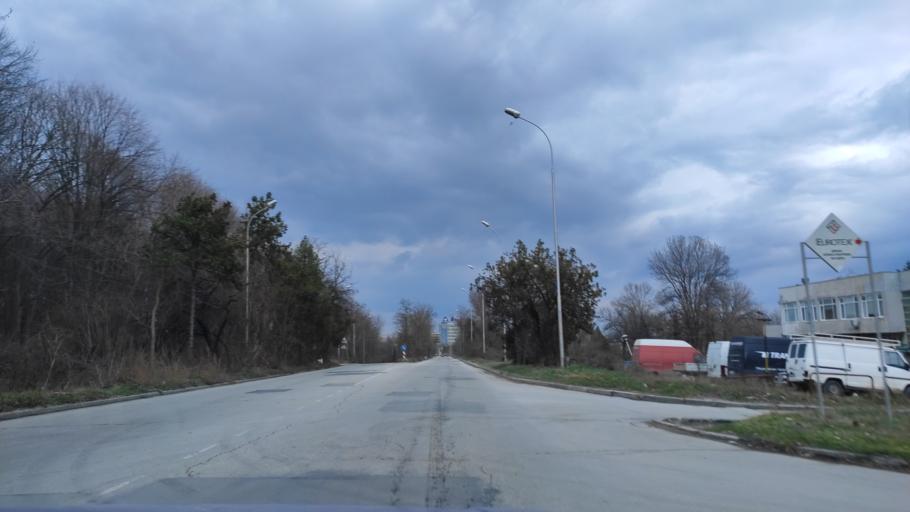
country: BG
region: Varna
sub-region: Obshtina Aksakovo
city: Aksakovo
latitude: 43.2244
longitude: 27.8636
